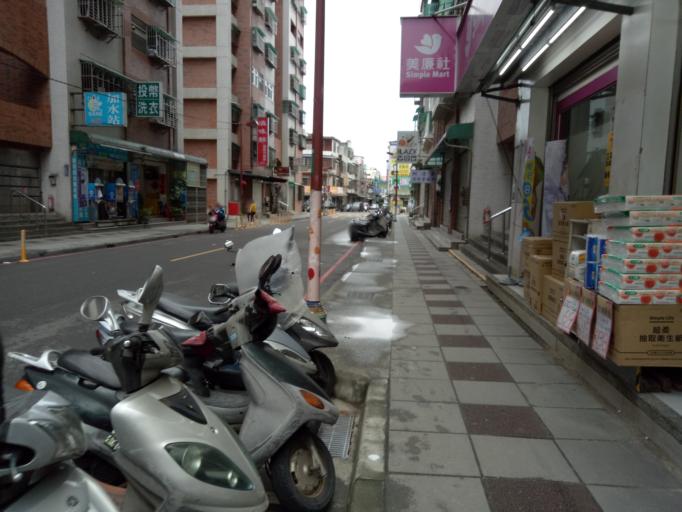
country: TW
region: Taiwan
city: Taoyuan City
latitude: 24.9615
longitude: 121.2978
